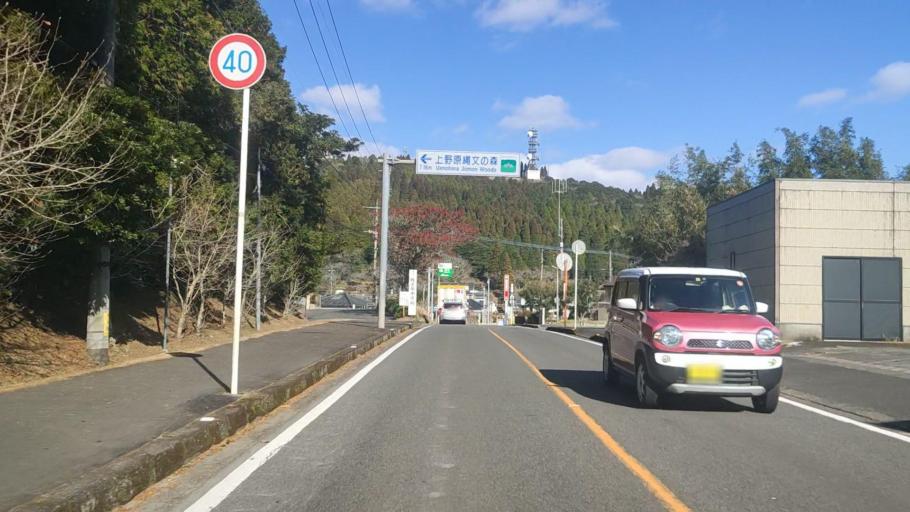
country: JP
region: Kagoshima
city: Kokubu-matsuki
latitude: 31.6710
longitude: 130.8456
